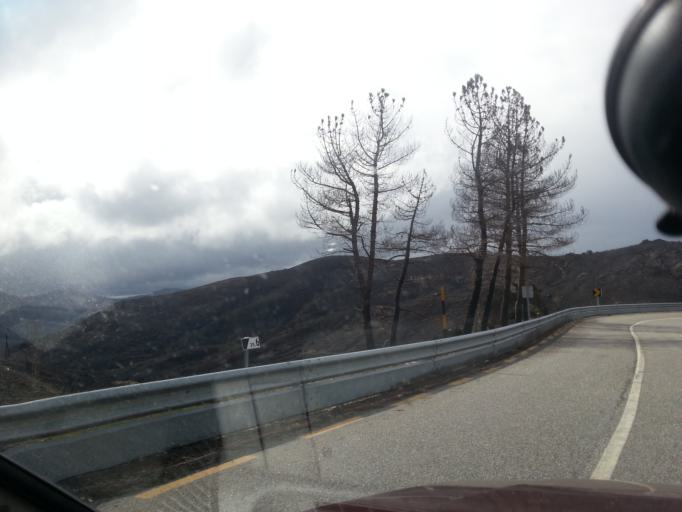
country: PT
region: Guarda
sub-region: Manteigas
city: Manteigas
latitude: 40.4215
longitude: -7.6157
